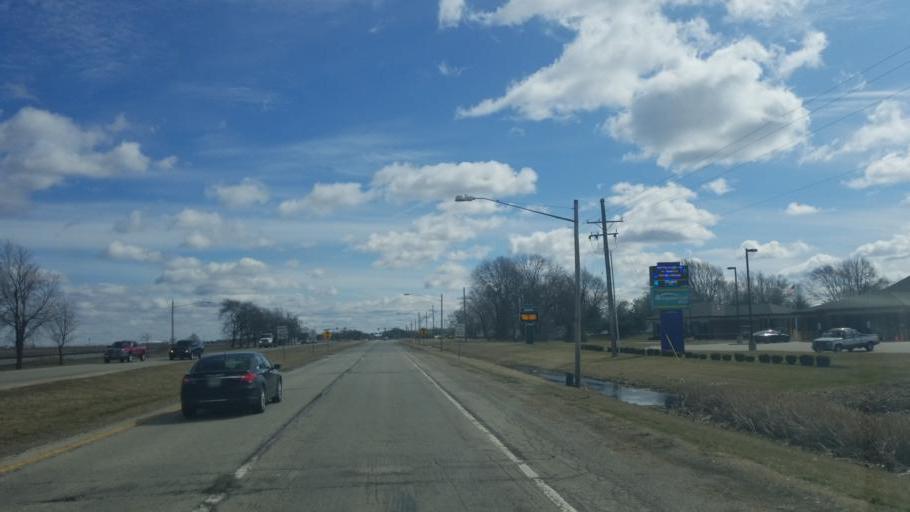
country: US
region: Illinois
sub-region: Macon County
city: Long Creek
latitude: 39.8230
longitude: -88.8871
